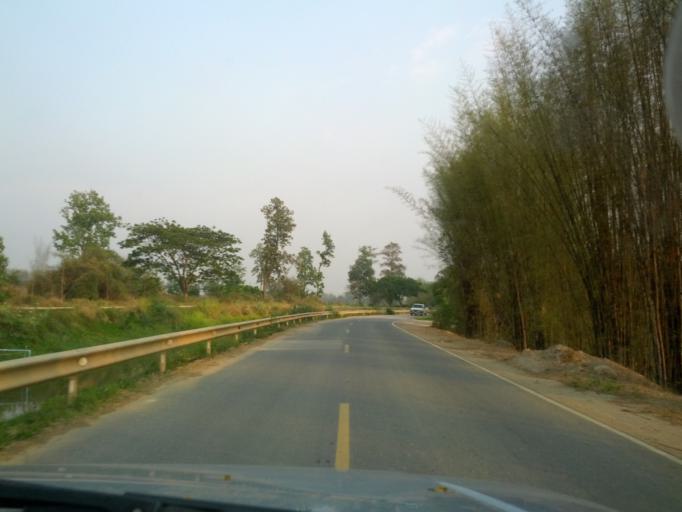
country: TH
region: Chiang Mai
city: San Sai
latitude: 18.9261
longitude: 98.9999
